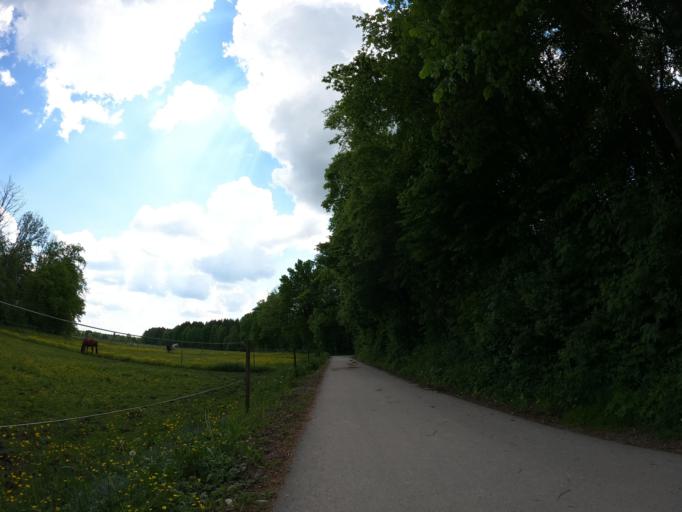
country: DE
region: Bavaria
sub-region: Upper Bavaria
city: Sauerlach
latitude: 47.9961
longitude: 11.6363
